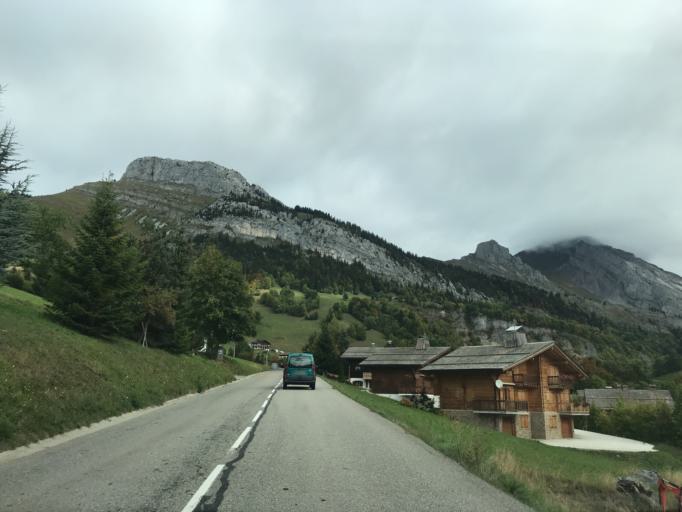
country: FR
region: Rhone-Alpes
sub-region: Departement de la Haute-Savoie
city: Le Grand-Bornand
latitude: 45.9581
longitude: 6.4380
